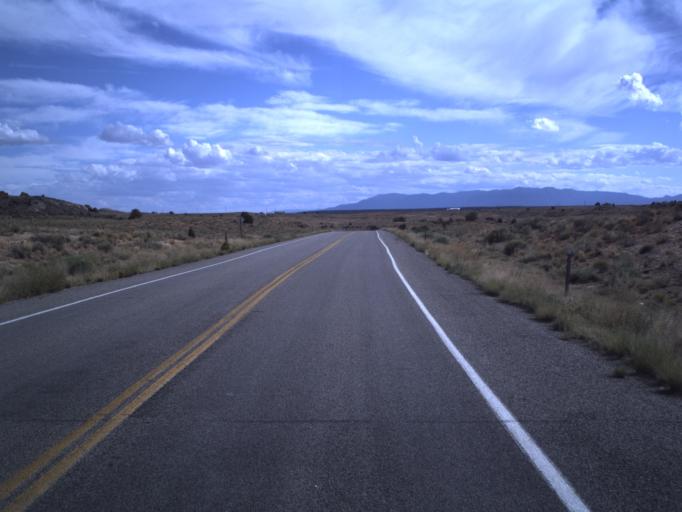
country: US
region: Colorado
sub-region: Montezuma County
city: Towaoc
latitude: 37.1897
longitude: -109.1274
